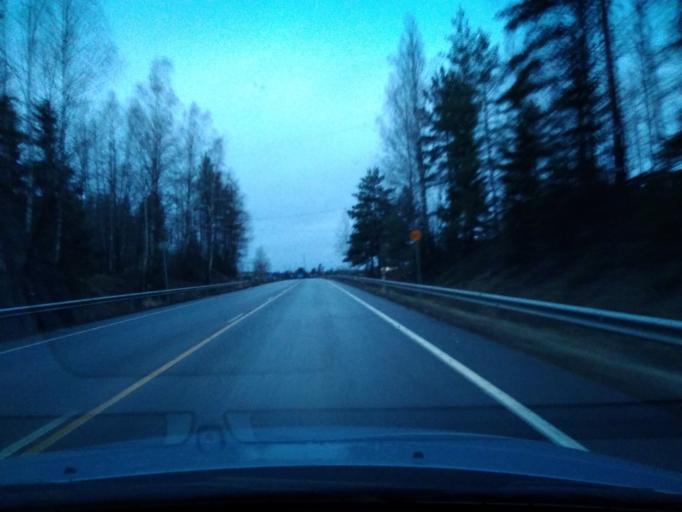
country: FI
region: Uusimaa
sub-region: Porvoo
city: Askola
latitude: 60.4915
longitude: 25.5560
